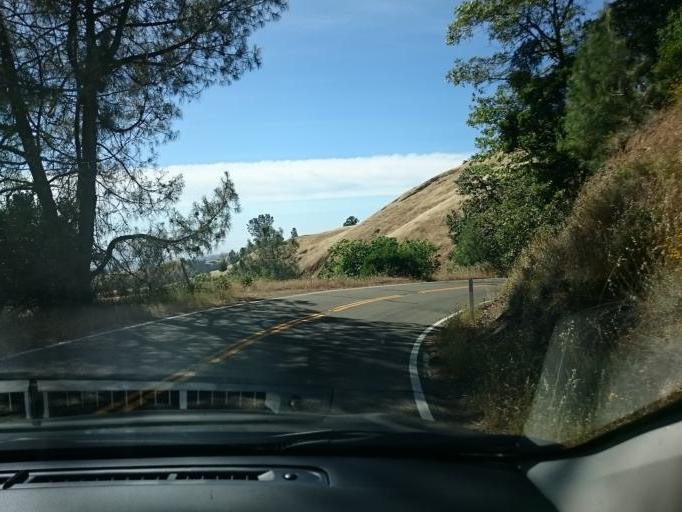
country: US
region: California
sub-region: Santa Clara County
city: East Foothills
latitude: 37.3393
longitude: -121.6570
